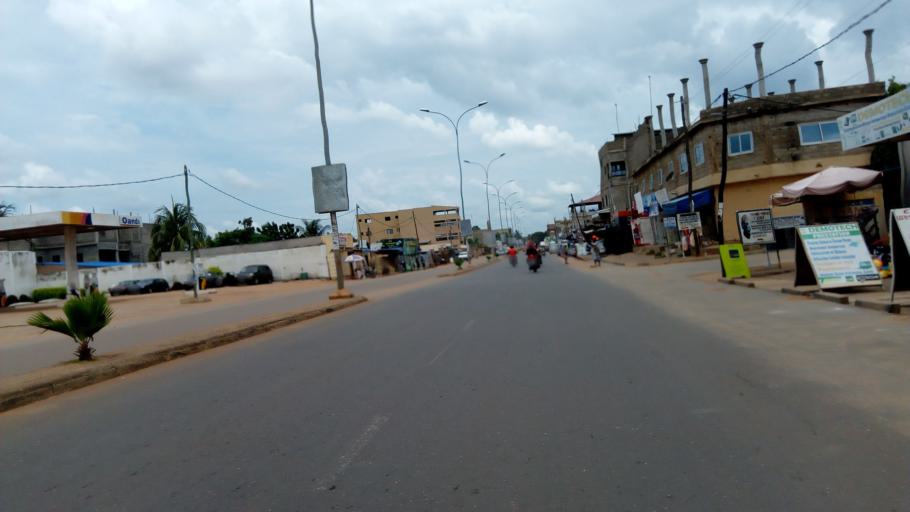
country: TG
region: Maritime
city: Lome
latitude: 6.2163
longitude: 1.1717
